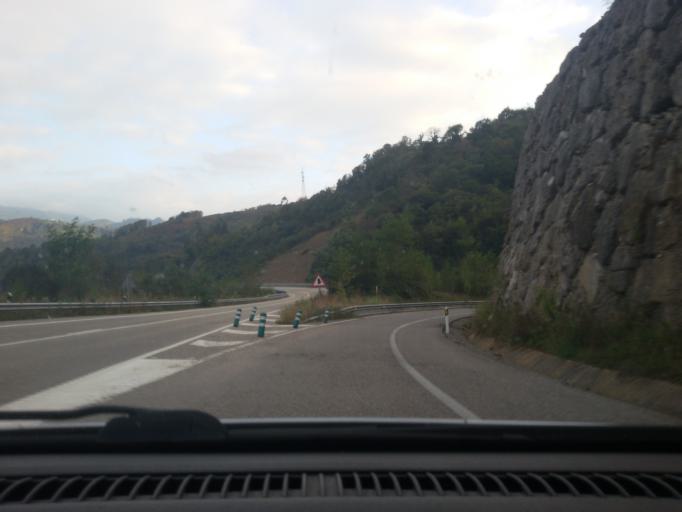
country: ES
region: Asturias
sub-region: Province of Asturias
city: Bimenes
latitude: 43.3435
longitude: -5.5827
